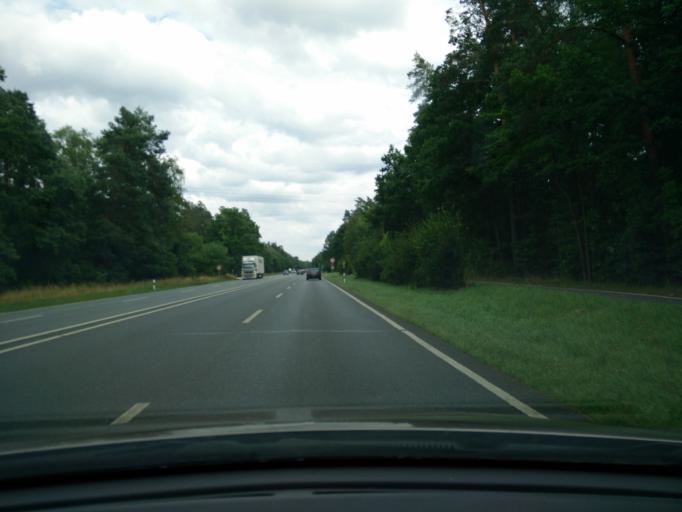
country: DE
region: Bavaria
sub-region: Regierungsbezirk Mittelfranken
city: Schwaig
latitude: 49.4231
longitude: 11.1534
